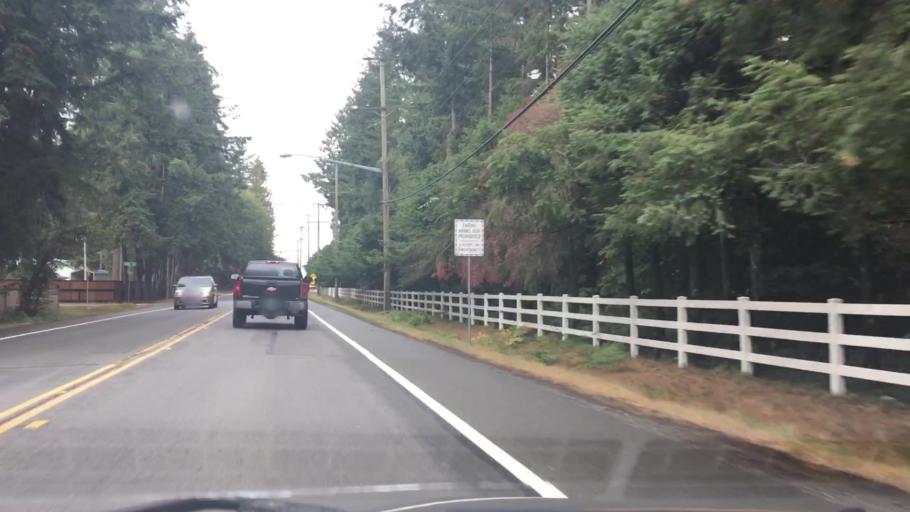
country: CA
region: British Columbia
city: Langley
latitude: 49.1041
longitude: -122.5612
